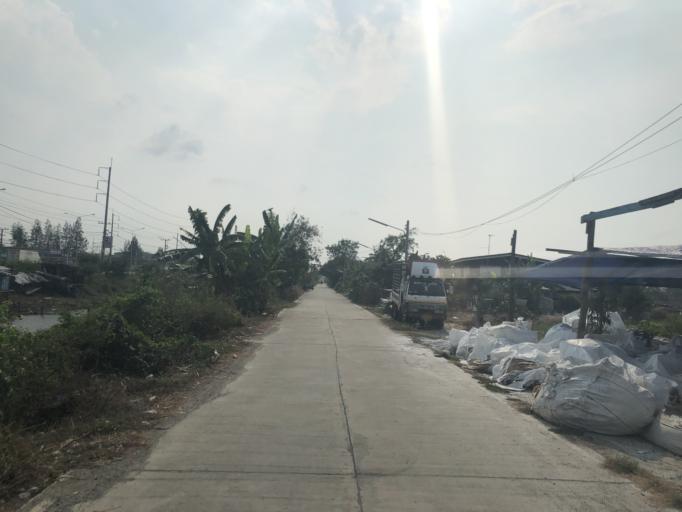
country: TH
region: Chachoengsao
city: Bang Pakong
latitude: 13.5042
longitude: 100.9747
